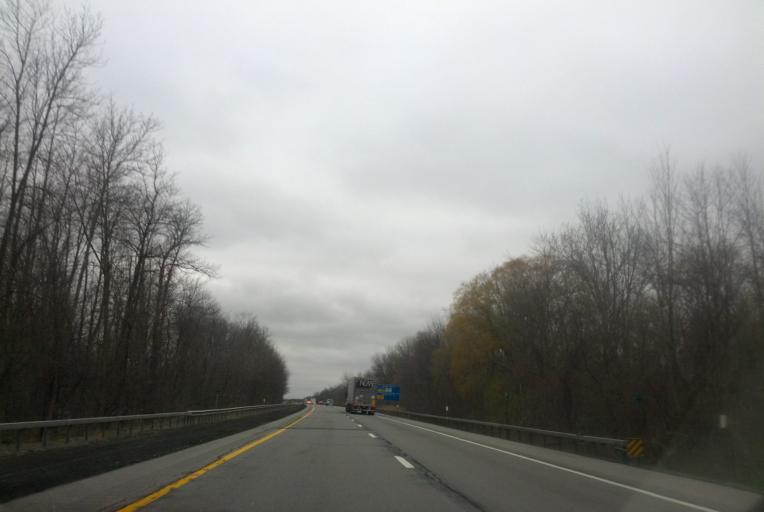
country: US
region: New York
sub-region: Ontario County
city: Manchester
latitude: 42.9778
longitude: -77.2107
